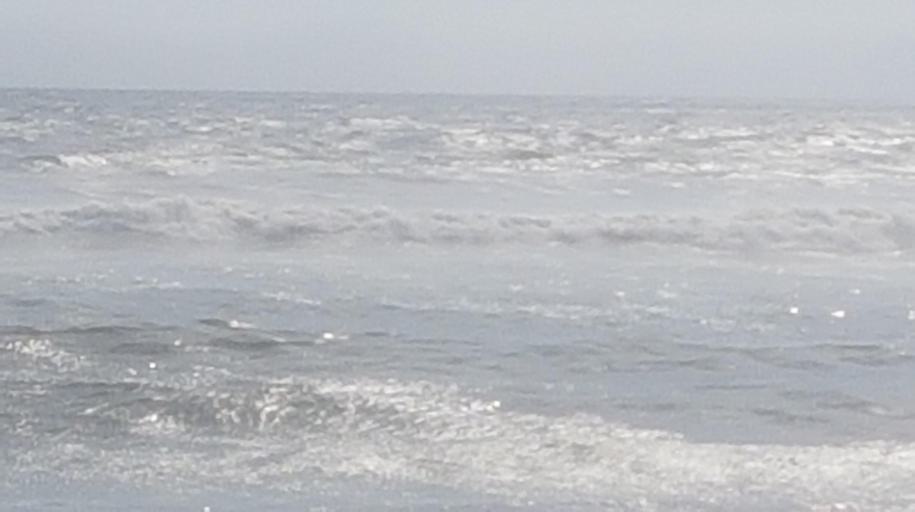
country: PE
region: La Libertad
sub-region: Viru
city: Chao
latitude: -8.6203
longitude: -78.7547
